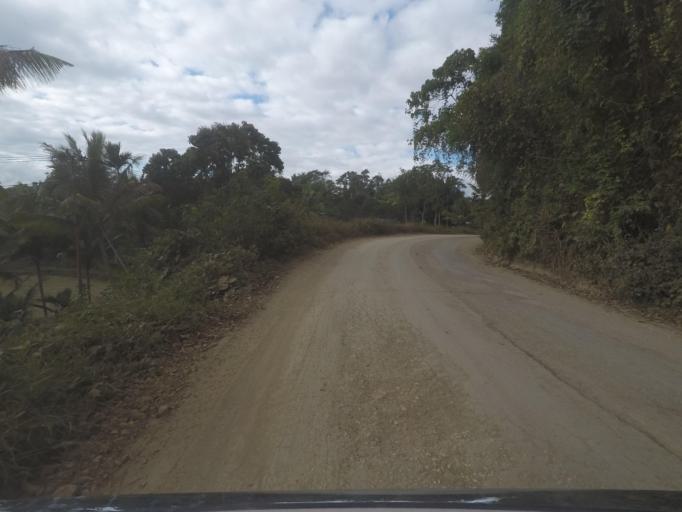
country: TL
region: Baucau
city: Venilale
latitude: -8.6083
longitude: 126.3824
